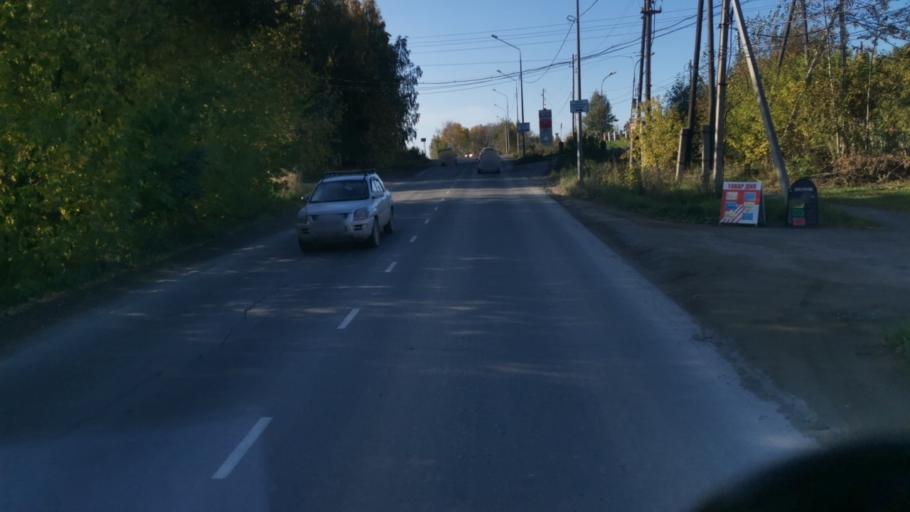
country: RU
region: Sverdlovsk
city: Nizhniy Tagil
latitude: 57.9398
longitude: 59.9267
